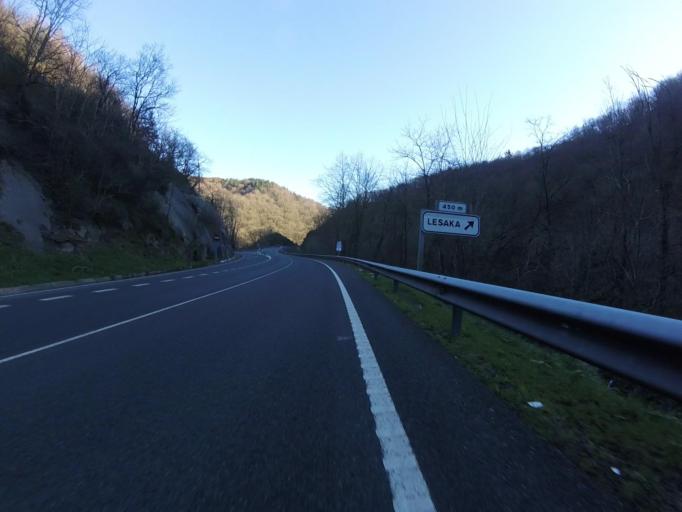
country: ES
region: Navarre
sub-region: Provincia de Navarra
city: Lesaka
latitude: 43.2613
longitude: -1.6840
